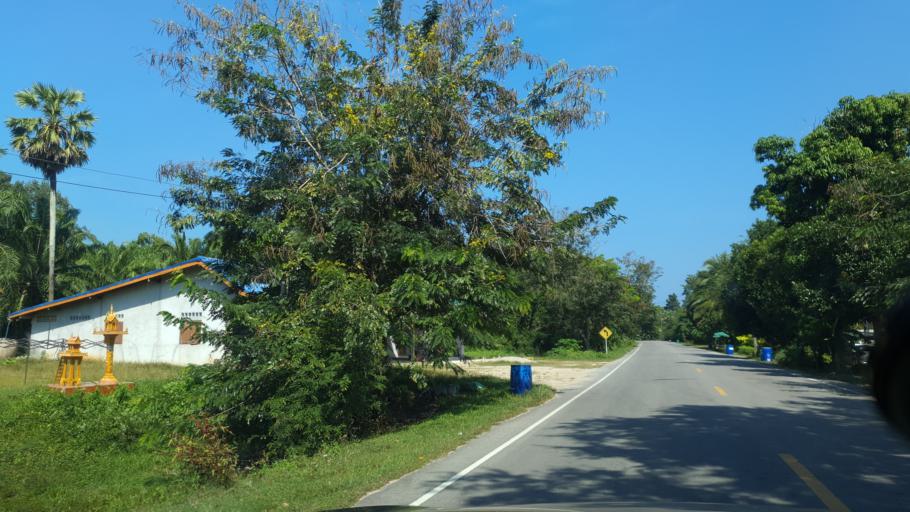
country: TH
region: Surat Thani
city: Tha Chana
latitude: 9.5833
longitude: 99.1969
